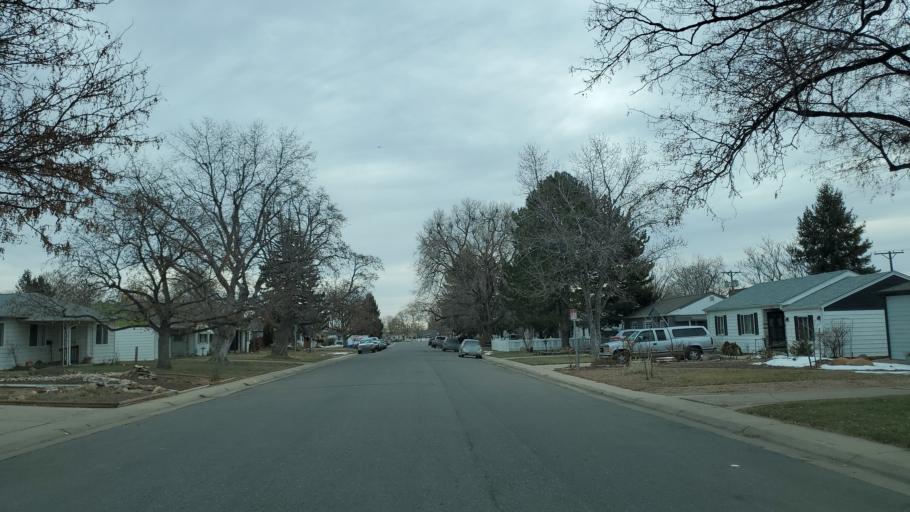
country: US
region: Colorado
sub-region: Denver County
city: Denver
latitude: 39.6982
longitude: -105.0084
